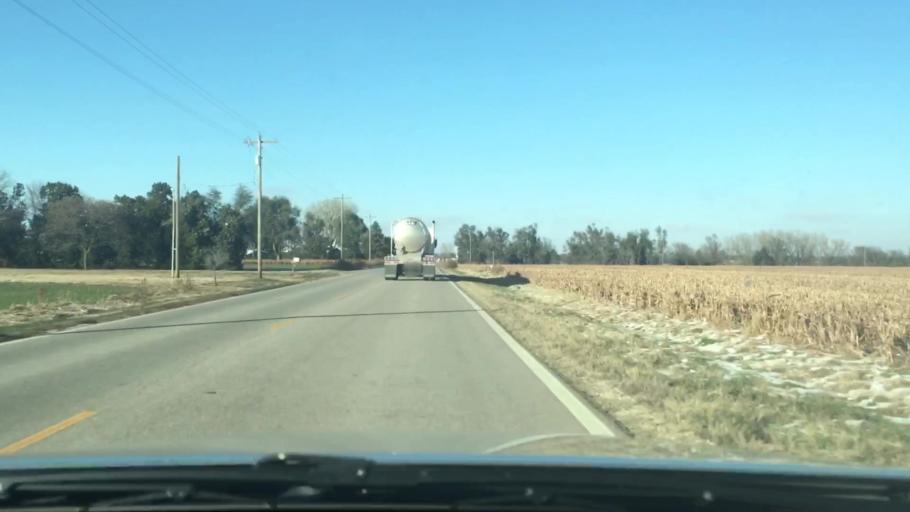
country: US
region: Kansas
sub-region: Rice County
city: Sterling
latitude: 38.1891
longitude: -98.2068
